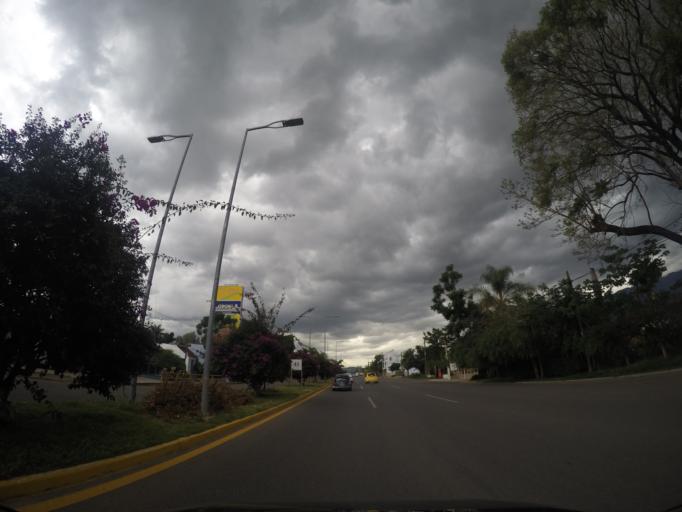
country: MX
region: Oaxaca
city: Tlalixtac de Cabrera
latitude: 17.0568
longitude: -96.6558
